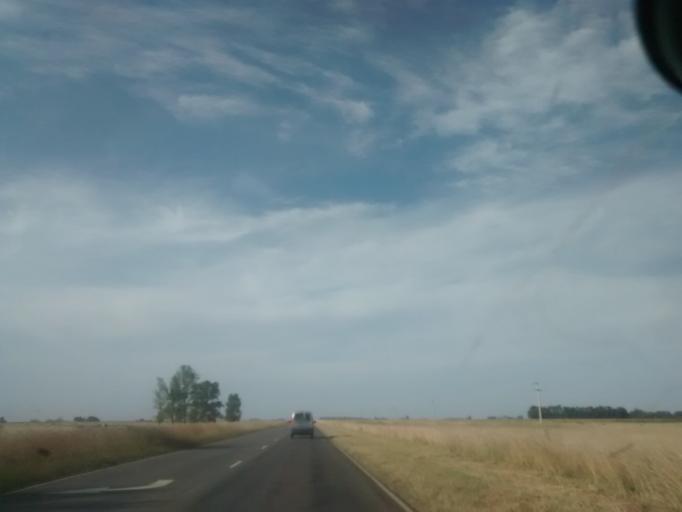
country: AR
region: Buenos Aires
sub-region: Partido de Ayacucho
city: Ayacucho
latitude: -37.1176
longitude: -58.5499
